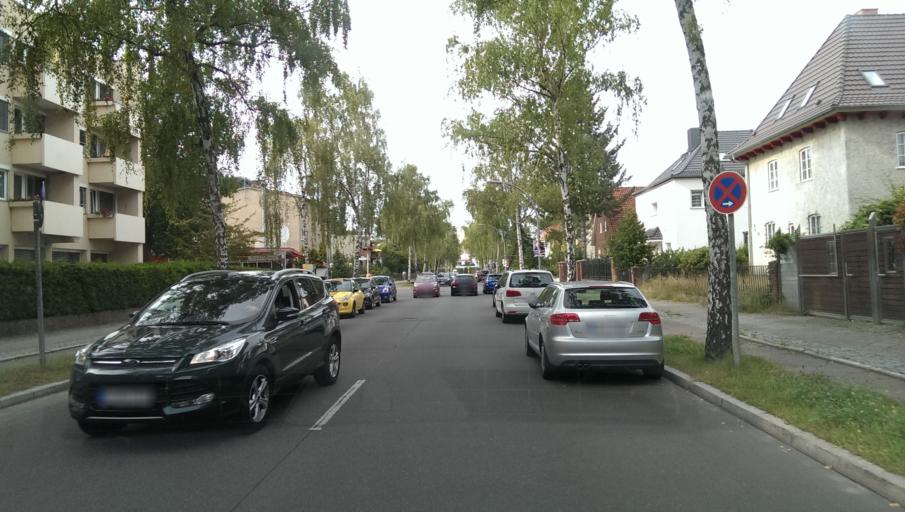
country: DE
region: Brandenburg
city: Teltow
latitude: 52.4165
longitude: 13.2509
